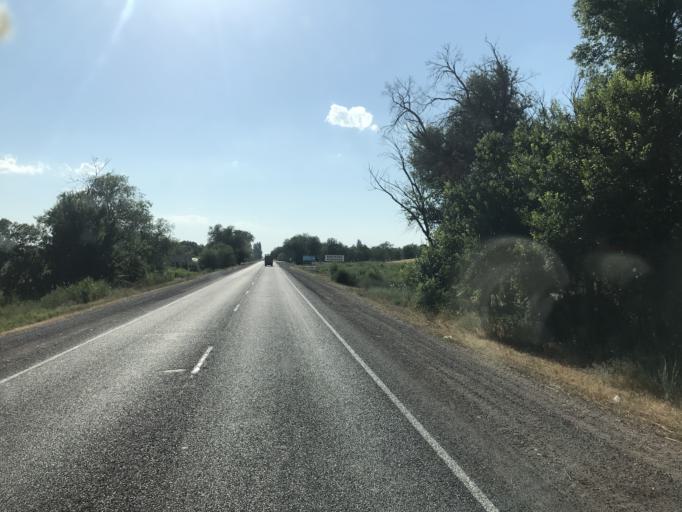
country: KZ
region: Zhambyl
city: Georgiyevka
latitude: 43.2260
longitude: 74.4086
